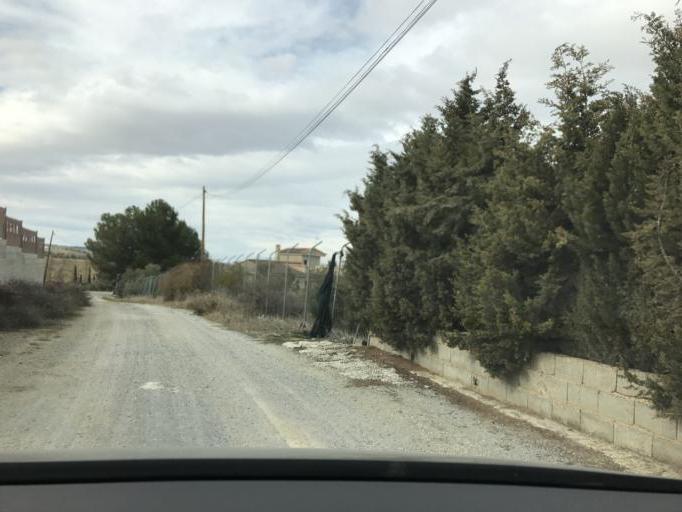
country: ES
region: Andalusia
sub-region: Provincia de Granada
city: Las Gabias
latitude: 37.1494
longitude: -3.6961
